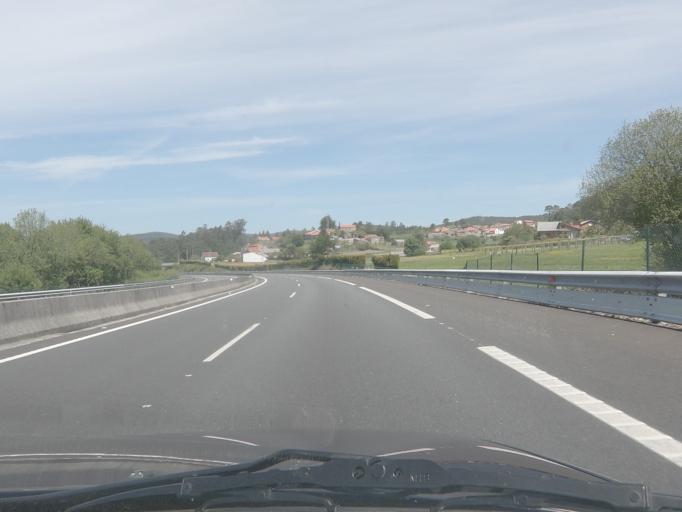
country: ES
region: Galicia
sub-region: Provincia de Pontevedra
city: Valga
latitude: 42.6637
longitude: -8.6343
